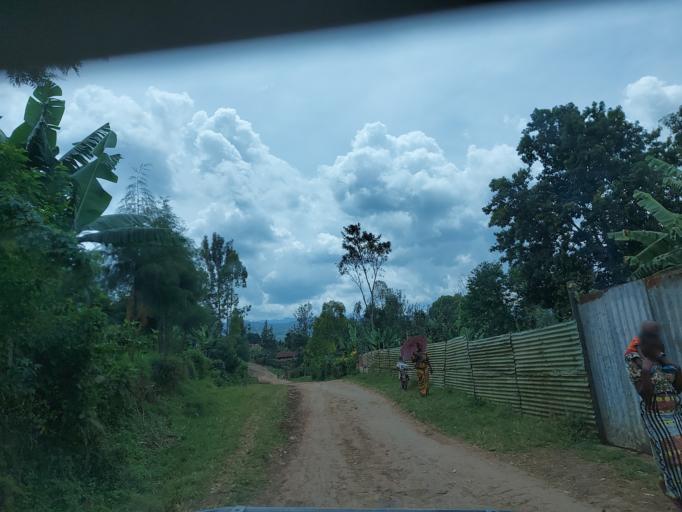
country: CD
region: South Kivu
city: Bukavu
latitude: -2.2442
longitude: 28.8192
